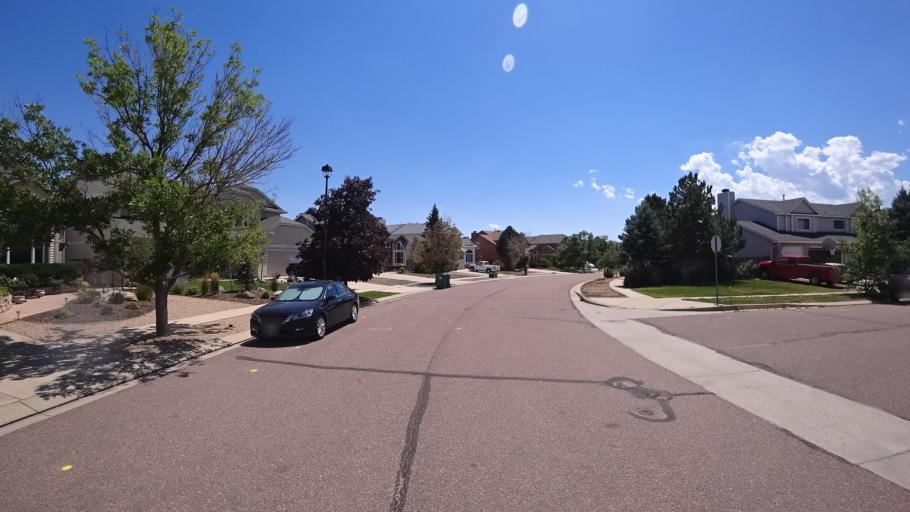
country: US
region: Colorado
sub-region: El Paso County
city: Black Forest
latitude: 38.9532
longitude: -104.7428
